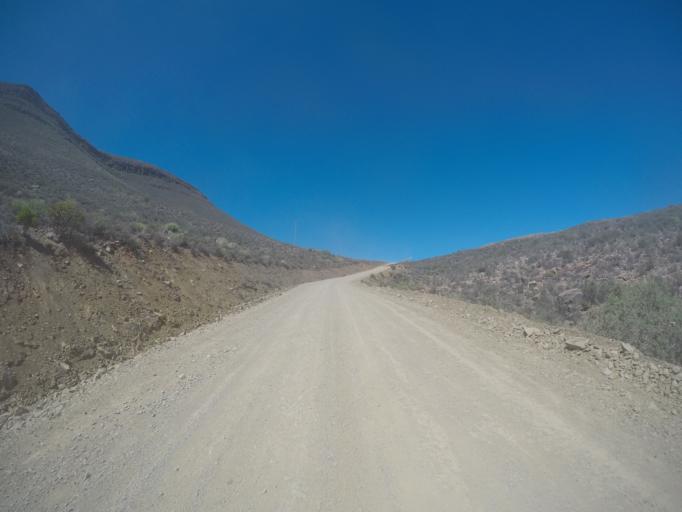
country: ZA
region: Western Cape
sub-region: West Coast District Municipality
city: Clanwilliam
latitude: -32.6041
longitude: 19.3686
